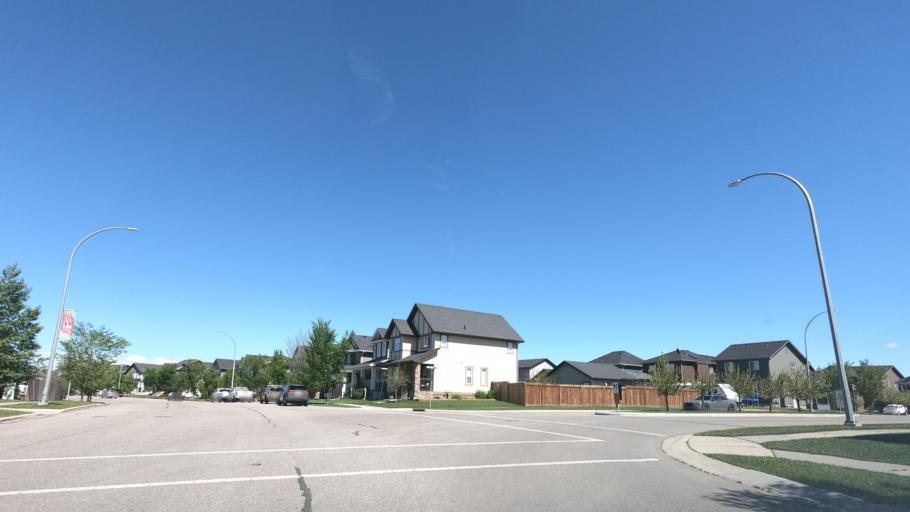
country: CA
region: Alberta
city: Airdrie
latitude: 51.2663
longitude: -113.9754
